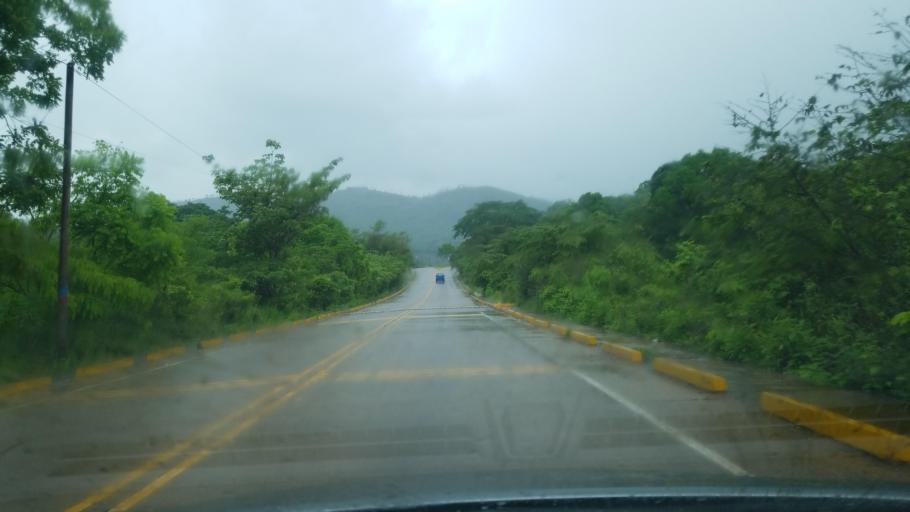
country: HN
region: Copan
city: Copan
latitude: 14.8365
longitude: -89.1607
